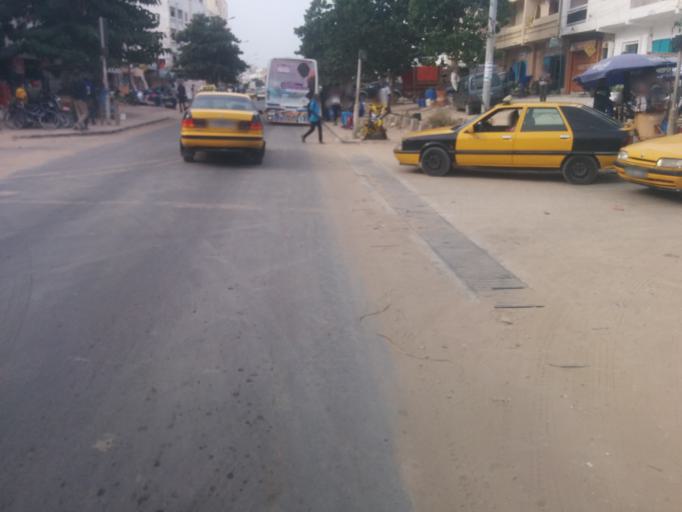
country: SN
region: Dakar
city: Grand Dakar
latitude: 14.7395
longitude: -17.4535
